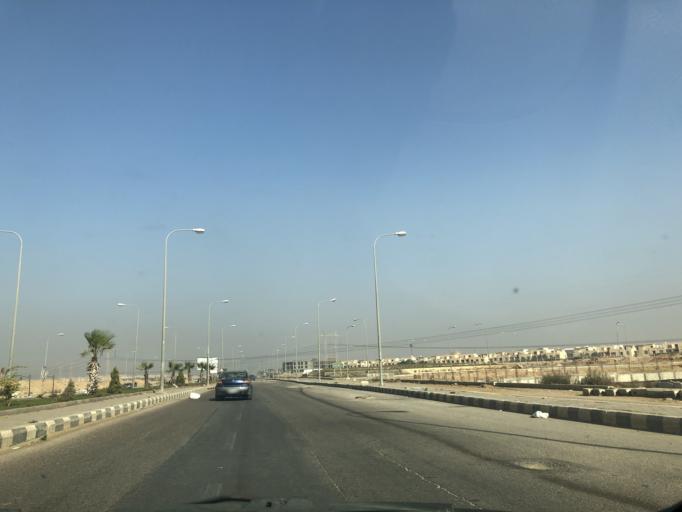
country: EG
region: Al Jizah
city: Madinat Sittah Uktubar
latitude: 29.9401
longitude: 31.0548
